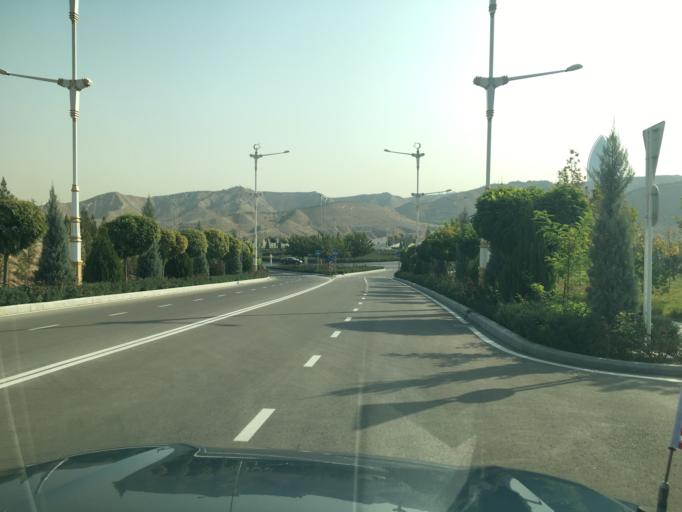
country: TM
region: Ahal
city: Ashgabat
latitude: 37.9367
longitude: 58.3198
